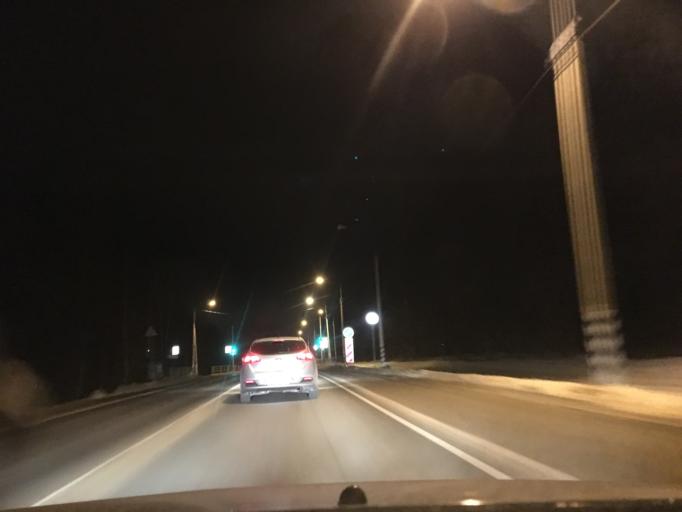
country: RU
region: Tula
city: Pervomayskiy
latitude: 54.0708
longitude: 37.5395
